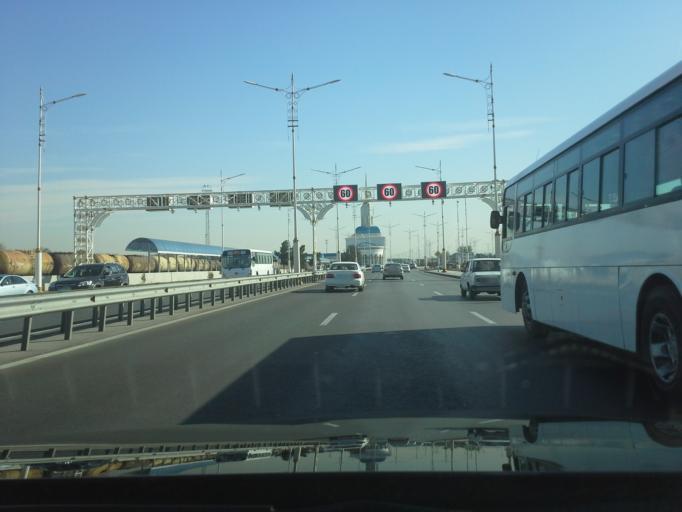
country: TM
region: Ahal
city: Ashgabat
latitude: 37.9450
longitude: 58.3919
